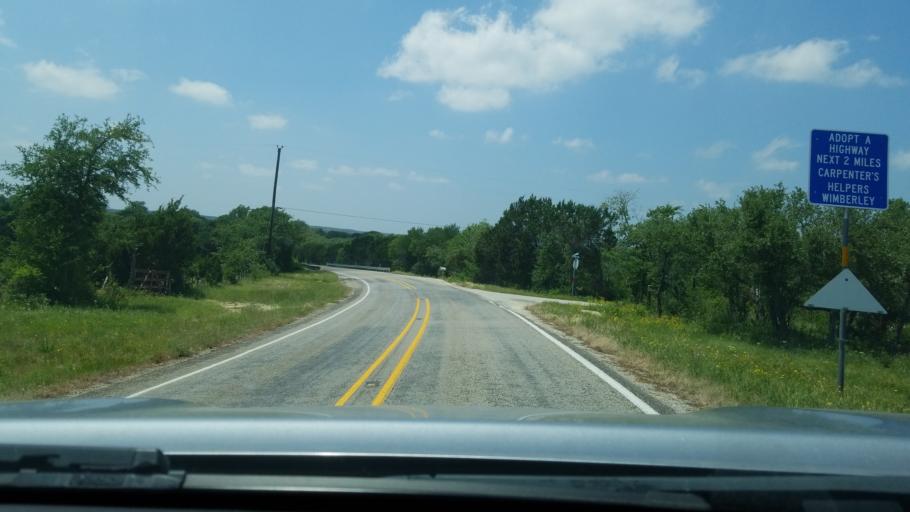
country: US
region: Texas
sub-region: Hays County
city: Woodcreek
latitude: 30.0978
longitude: -98.2393
